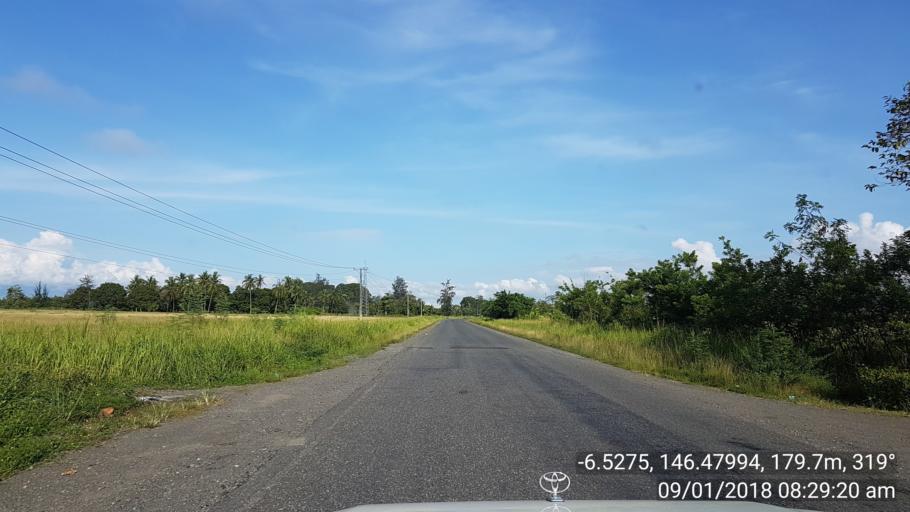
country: PG
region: Morobe
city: Lae
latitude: -6.5275
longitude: 146.4800
